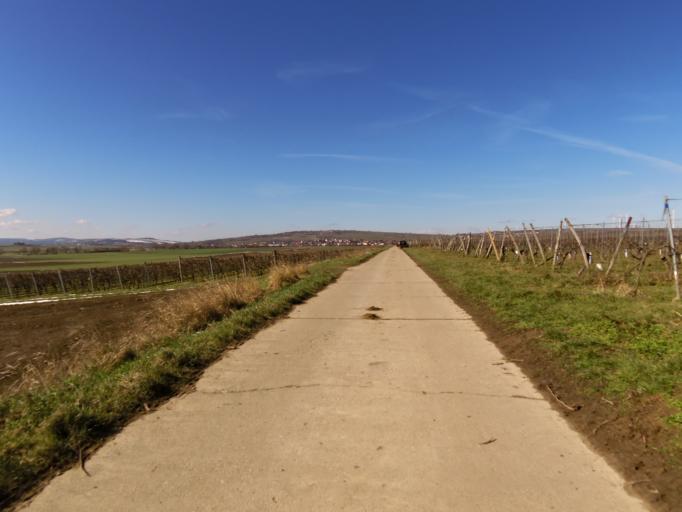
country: DE
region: Rheinland-Pfalz
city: Hohen-Sulzen
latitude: 49.6149
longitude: 8.2106
